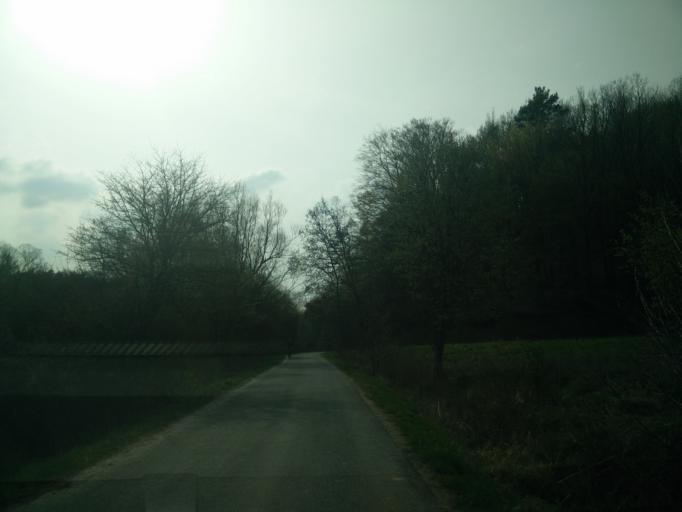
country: SK
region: Nitriansky
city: Prievidza
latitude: 48.8220
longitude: 18.6730
